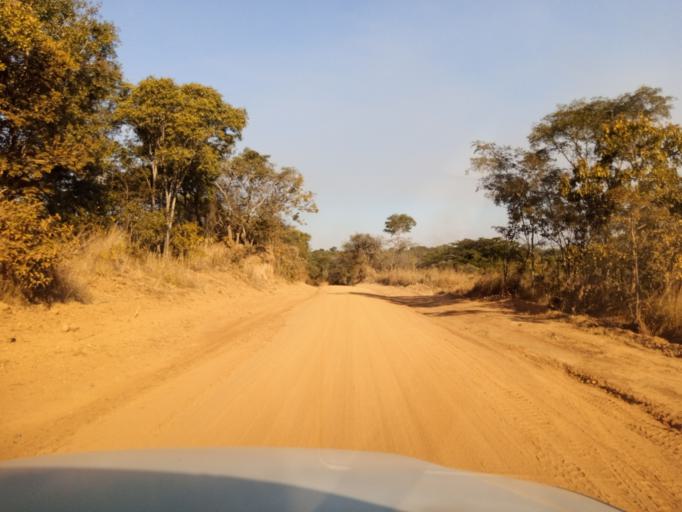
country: CD
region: Katanga
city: Lubumbashi
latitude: -11.3020
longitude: 27.2813
